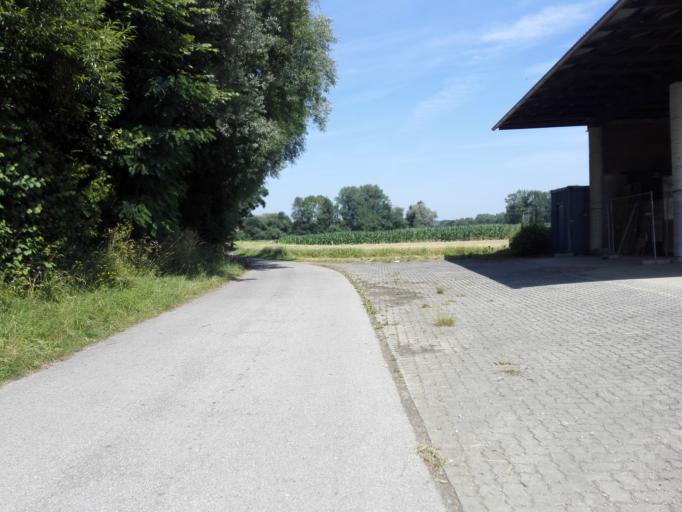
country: AT
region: Styria
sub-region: Politischer Bezirk Graz-Umgebung
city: Gossendorf
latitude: 46.9904
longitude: 15.4652
